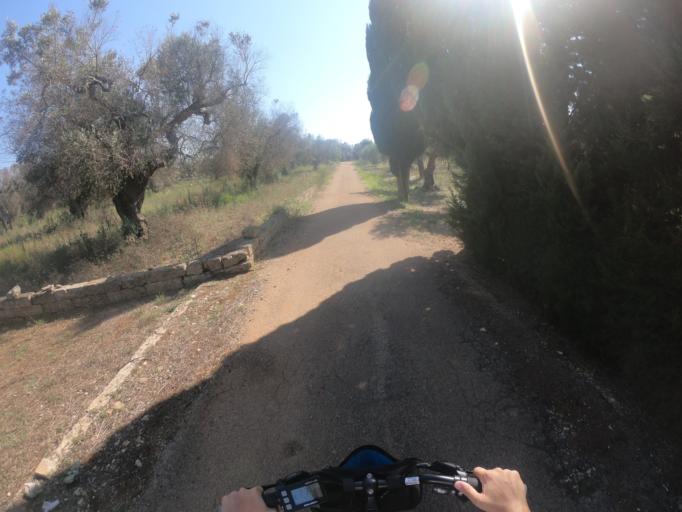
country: IT
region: Apulia
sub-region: Provincia di Lecce
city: Specchia
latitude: 39.9183
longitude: 18.2856
